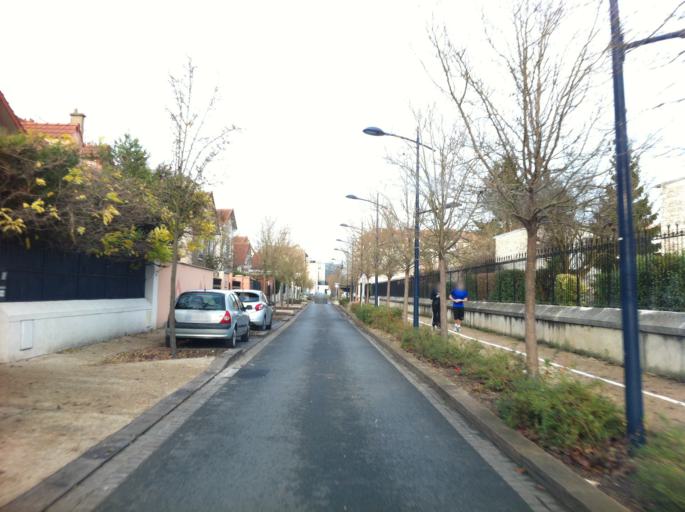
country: FR
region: Ile-de-France
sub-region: Departement de Seine-et-Marne
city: Dammarie-les-Lys
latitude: 48.5210
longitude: 2.6429
